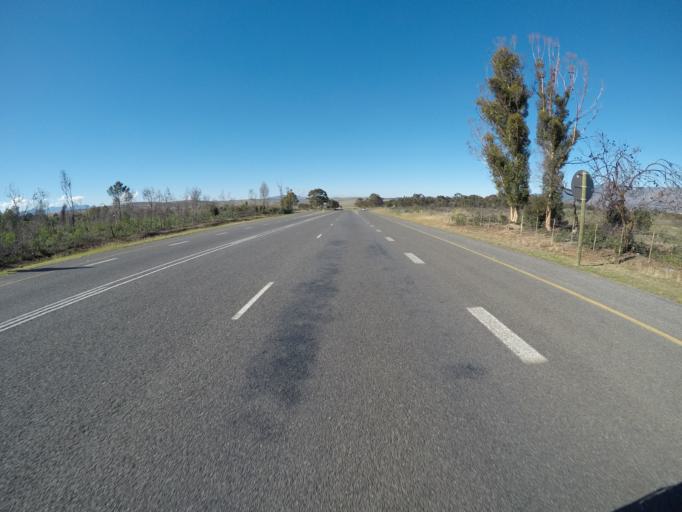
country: ZA
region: Western Cape
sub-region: Overberg District Municipality
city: Hermanus
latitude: -34.2352
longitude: 19.1978
